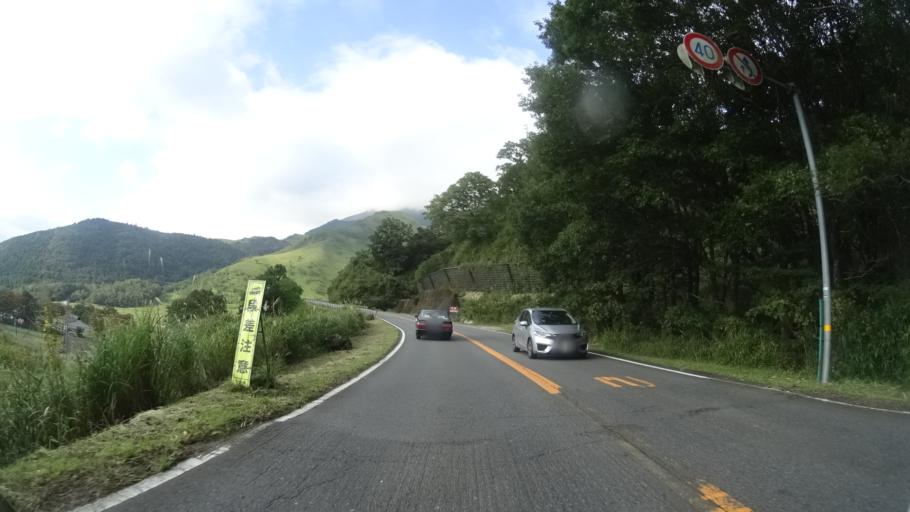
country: JP
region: Oita
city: Beppu
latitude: 33.2585
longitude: 131.3811
